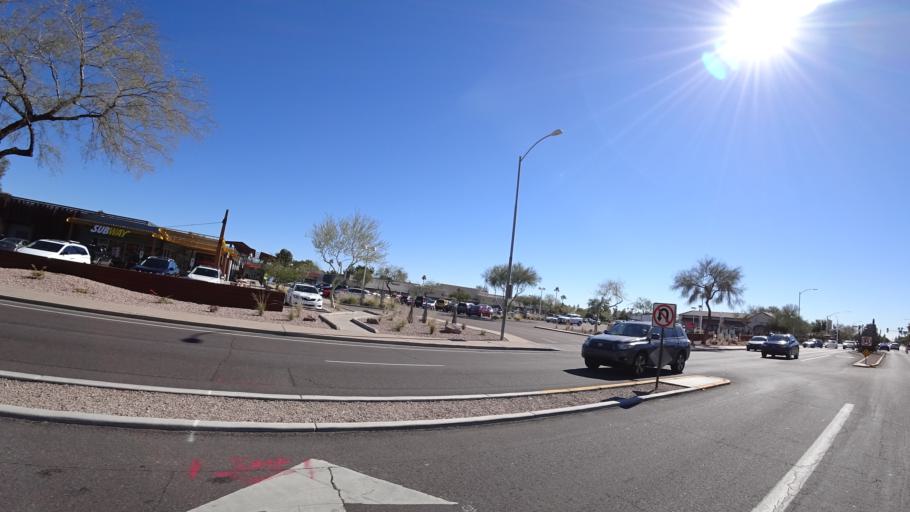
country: US
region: Arizona
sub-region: Maricopa County
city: Scottsdale
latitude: 33.4965
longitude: -111.9175
